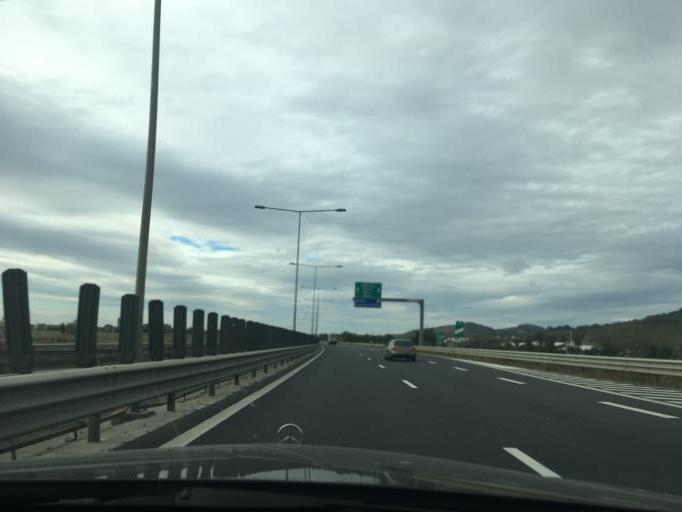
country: RO
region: Sibiu
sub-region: Comuna Selimbar
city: Selimbar
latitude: 45.7951
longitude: 24.1955
